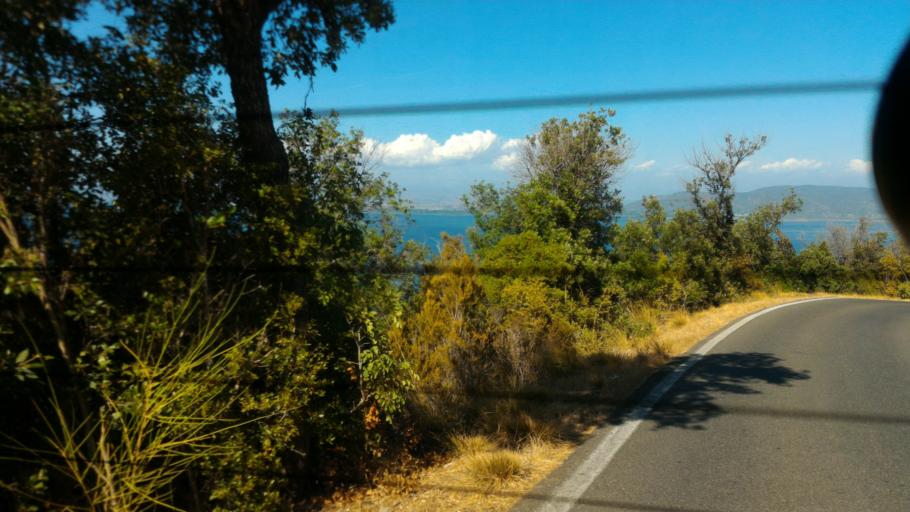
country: IT
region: Tuscany
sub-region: Provincia di Grosseto
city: Monte Argentario
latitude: 42.4225
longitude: 11.1632
